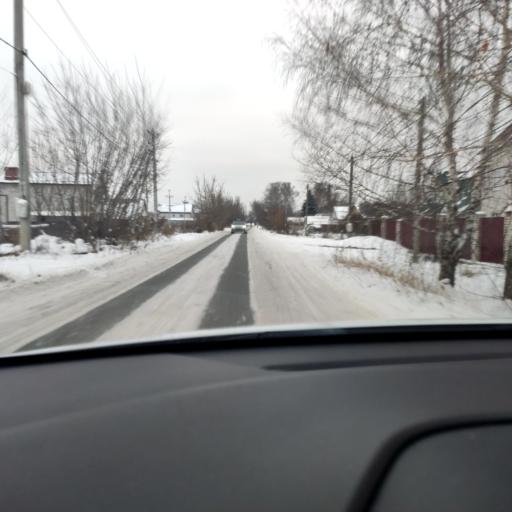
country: RU
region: Tatarstan
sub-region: Gorod Kazan'
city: Kazan
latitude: 55.8732
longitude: 49.1498
